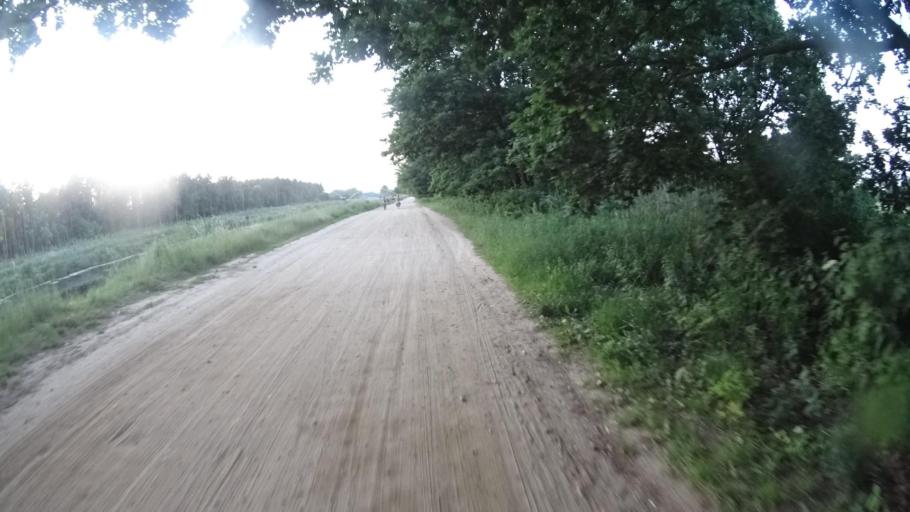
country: PL
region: Masovian Voivodeship
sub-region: Powiat legionowski
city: Stanislawow Pierwszy
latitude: 52.3489
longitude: 21.0344
